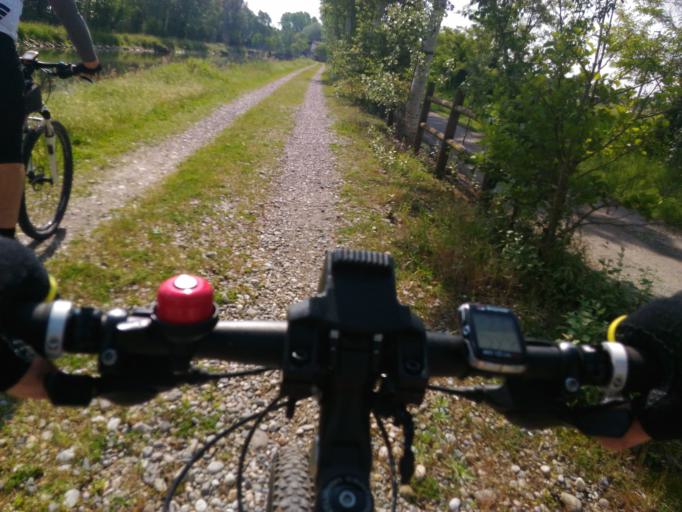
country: IT
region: Lombardy
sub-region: Provincia di Lodi
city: Massalengo-Motta Vigana
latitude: 45.2736
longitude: 9.5000
